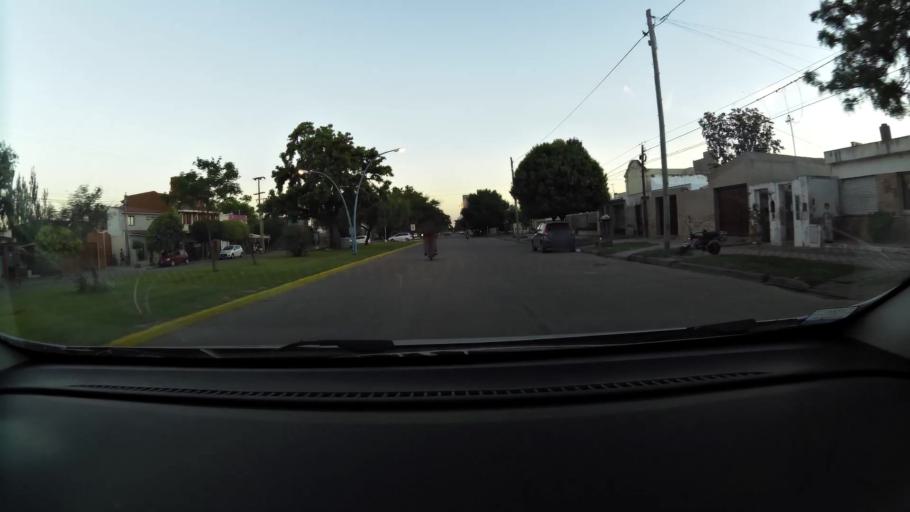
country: AR
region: Cordoba
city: Villa Maria
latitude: -32.4106
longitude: -63.2555
